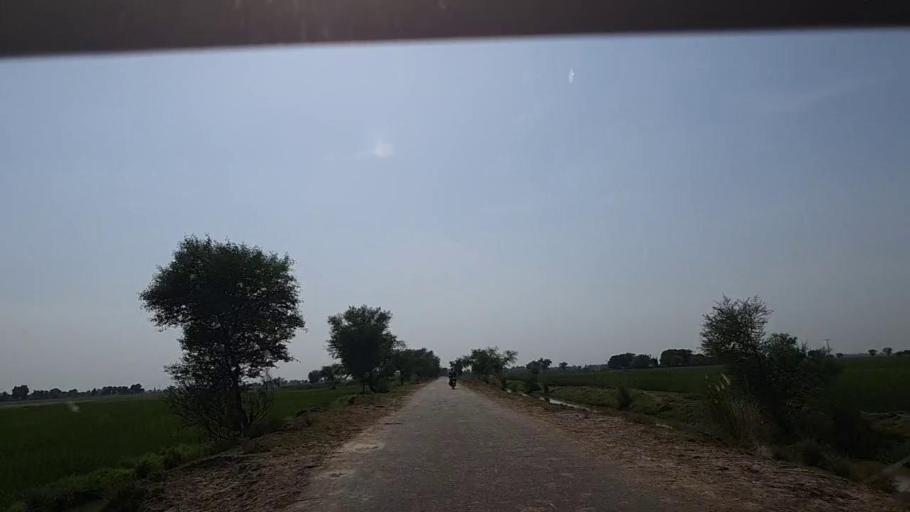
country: PK
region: Sindh
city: Khanpur
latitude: 27.8431
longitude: 69.3860
